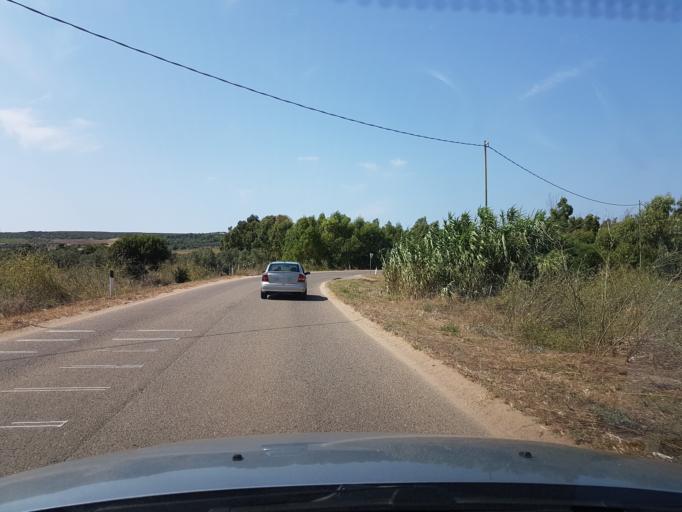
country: IT
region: Sardinia
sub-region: Provincia di Oristano
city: Cabras
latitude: 39.9174
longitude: 8.4514
